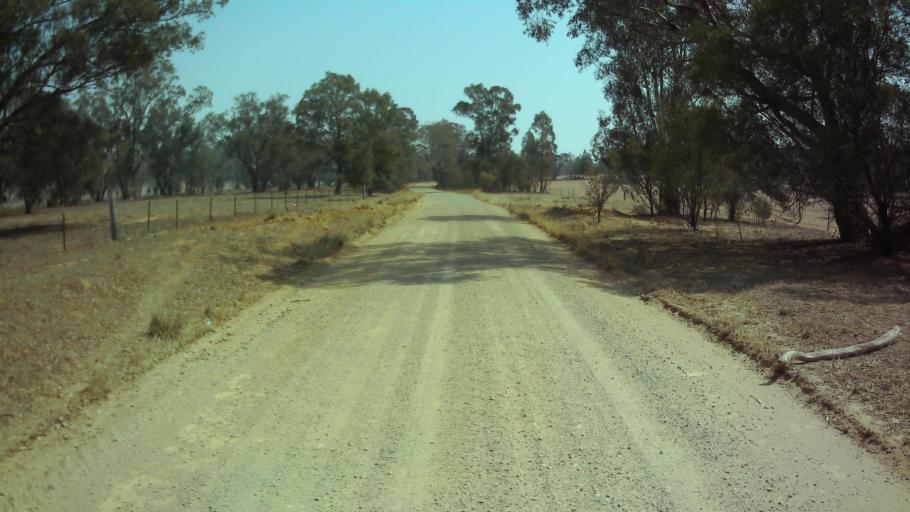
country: AU
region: New South Wales
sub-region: Weddin
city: Grenfell
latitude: -33.6673
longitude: 148.2747
